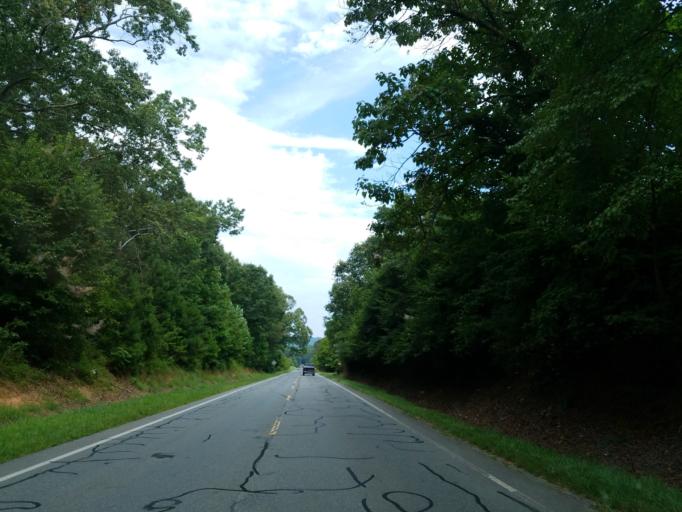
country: US
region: Georgia
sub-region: Gilmer County
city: Ellijay
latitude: 34.6405
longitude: -84.5370
